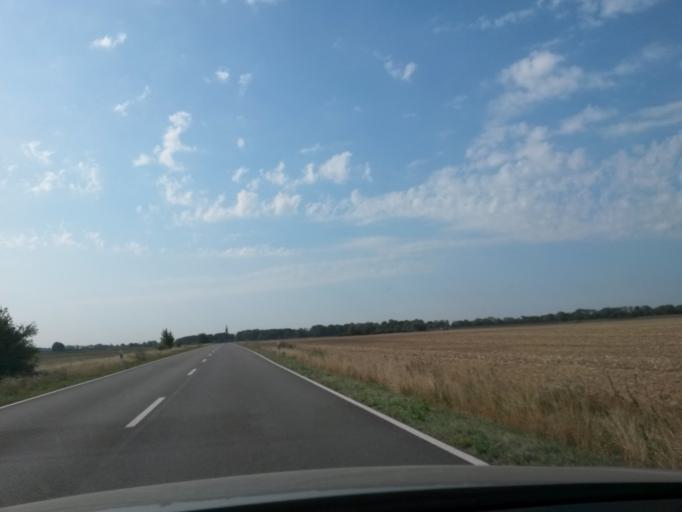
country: DE
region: Saxony-Anhalt
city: Jerichow
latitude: 52.5194
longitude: 12.0158
